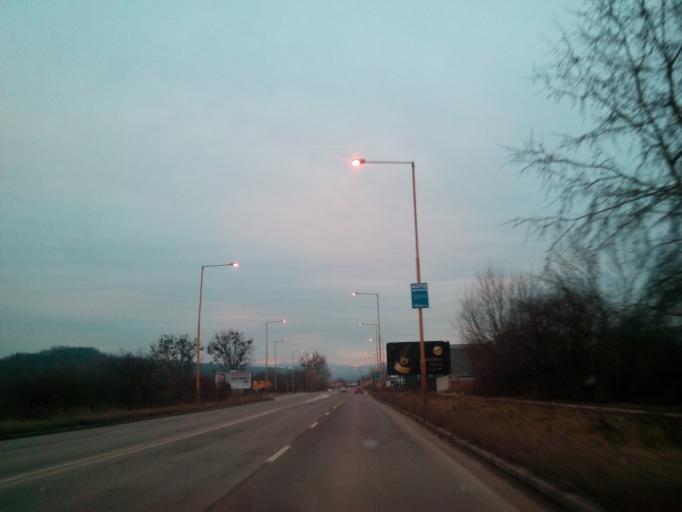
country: SK
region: Kosicky
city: Kosice
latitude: 48.6991
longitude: 21.2250
